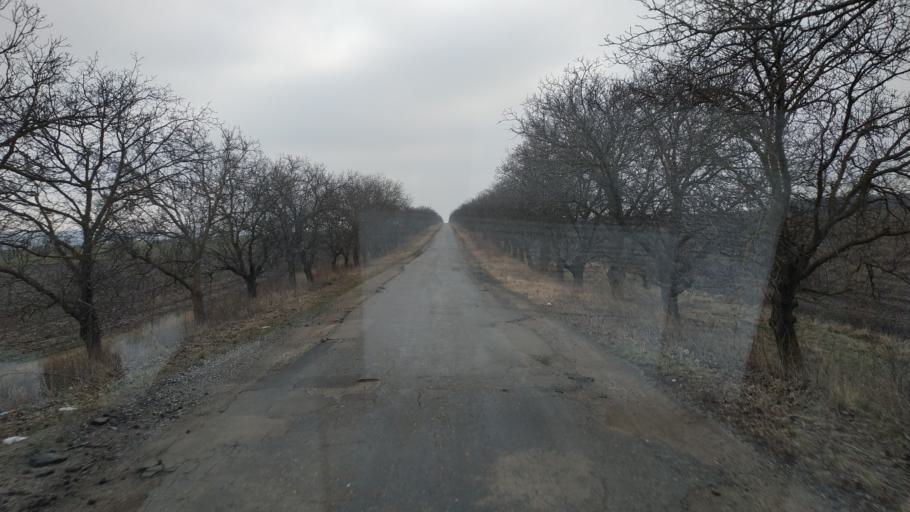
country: MD
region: Hincesti
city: Dancu
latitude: 46.8994
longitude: 28.3047
